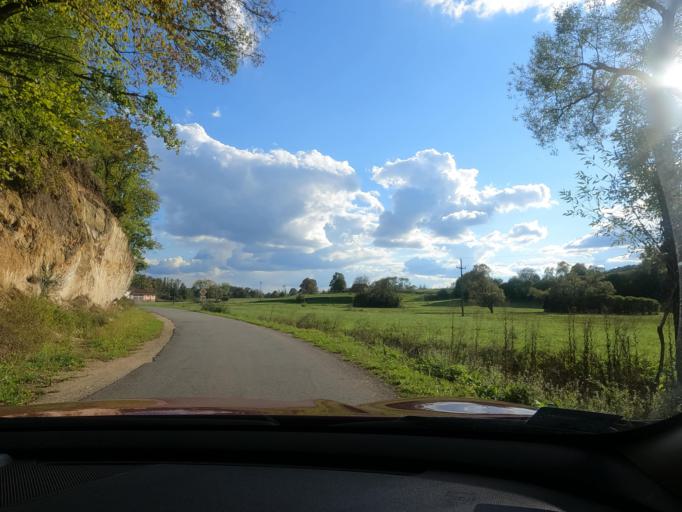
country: HR
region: Sisacko-Moslavacka
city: Petrinja
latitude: 45.3850
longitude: 16.2480
